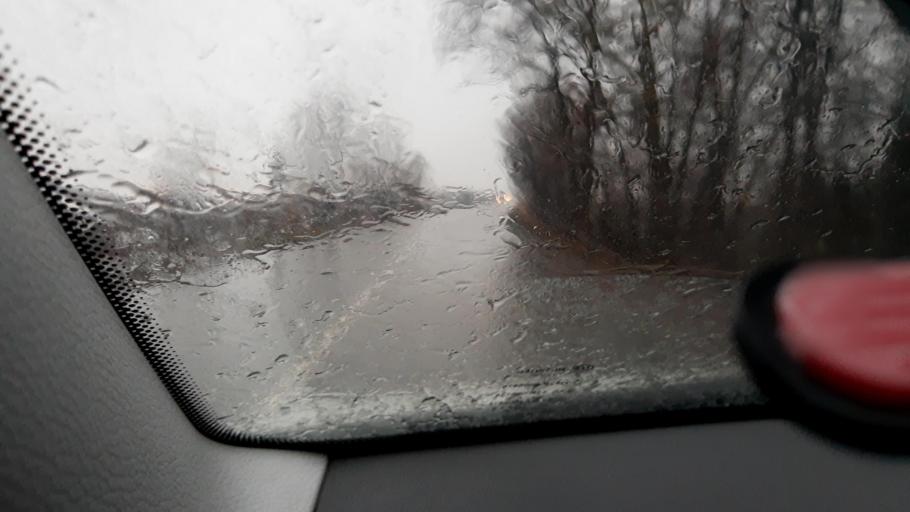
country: RU
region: Bashkortostan
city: Iglino
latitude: 54.9005
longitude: 56.1891
